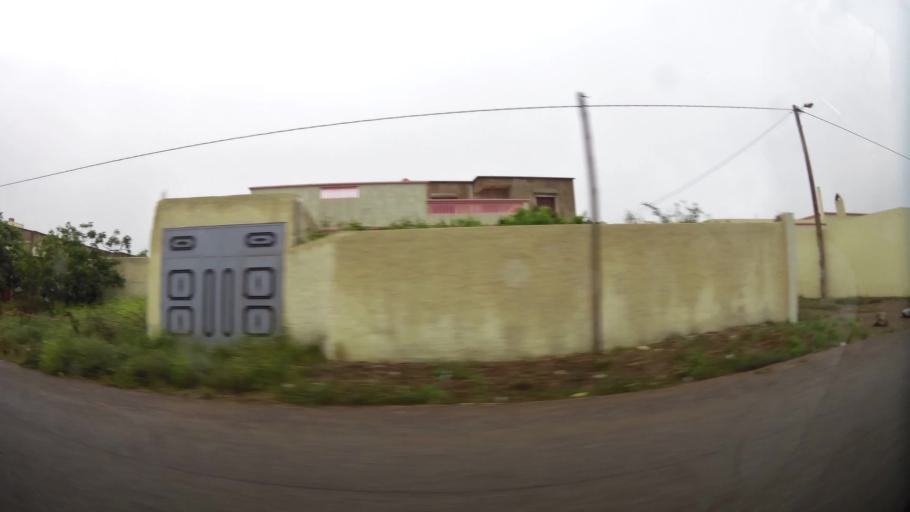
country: MA
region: Oriental
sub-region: Nador
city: Boudinar
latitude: 35.1256
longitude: -3.5780
